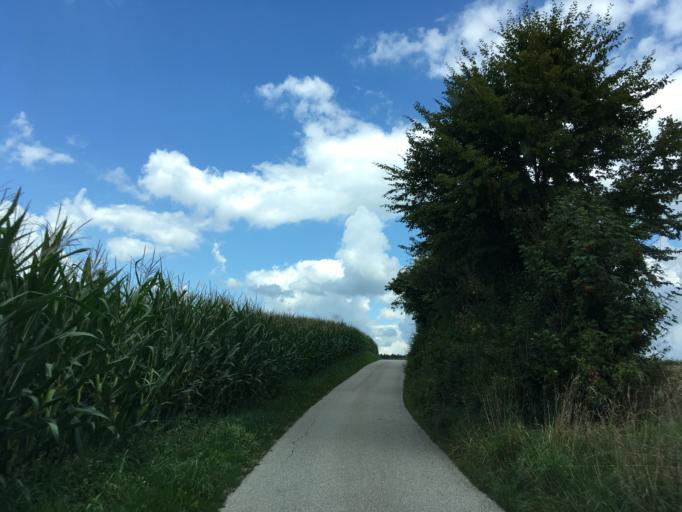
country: DE
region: Bavaria
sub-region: Upper Bavaria
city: Schnaitsee
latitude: 48.0490
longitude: 12.3357
